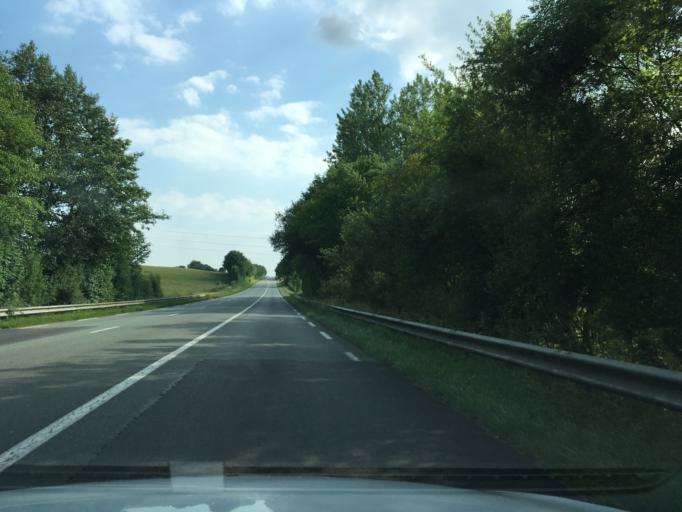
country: FR
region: Poitou-Charentes
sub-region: Departement des Deux-Sevres
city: Saint-Pardoux
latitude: 46.5609
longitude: -0.3039
